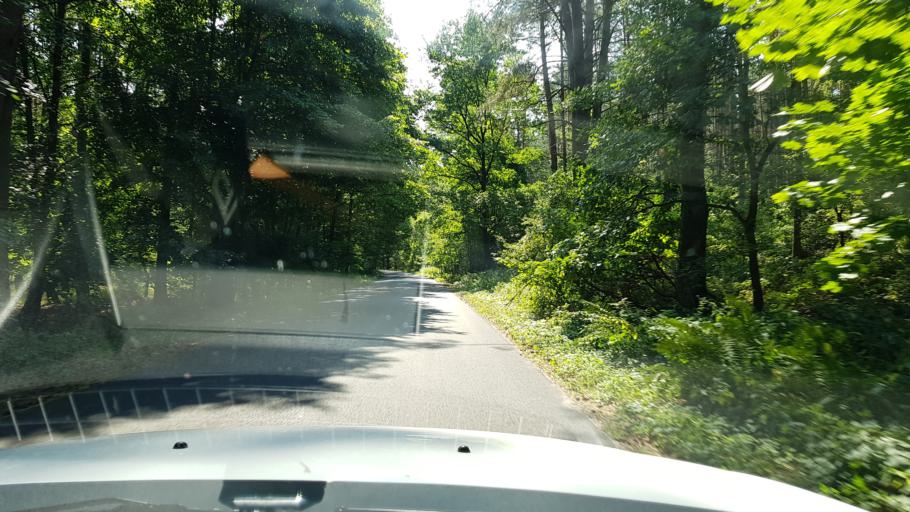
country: PL
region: West Pomeranian Voivodeship
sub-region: Powiat gryfinski
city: Chojna
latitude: 52.9393
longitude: 14.5151
